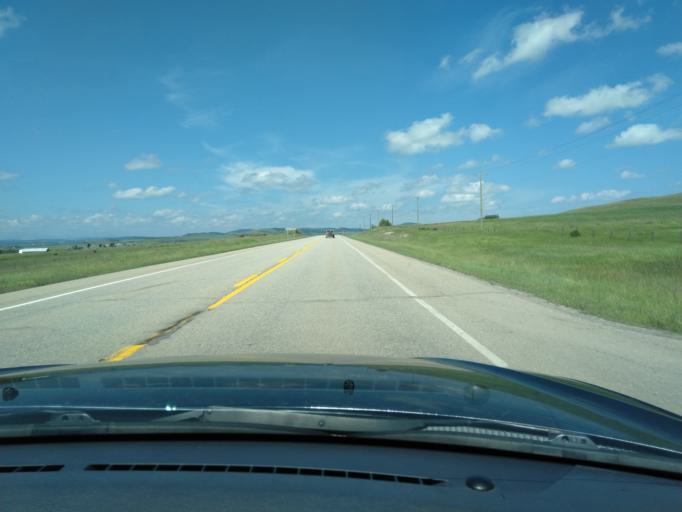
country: CA
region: Alberta
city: Cochrane
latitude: 51.2165
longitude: -114.5363
